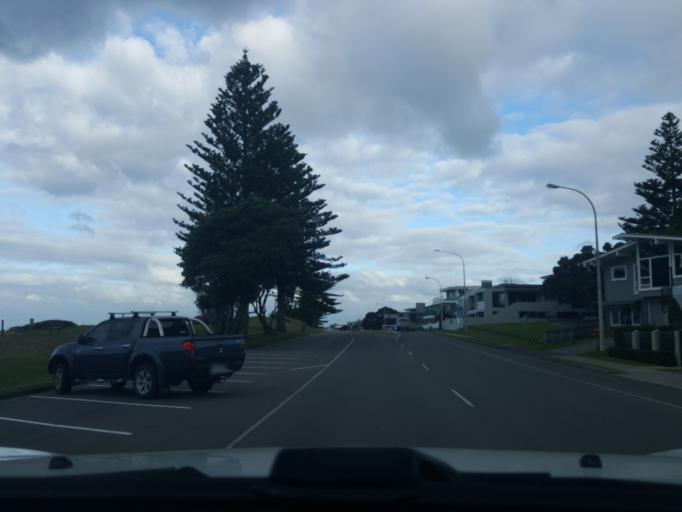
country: NZ
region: Bay of Plenty
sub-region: Tauranga City
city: Tauranga
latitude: -37.6382
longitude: 176.1888
